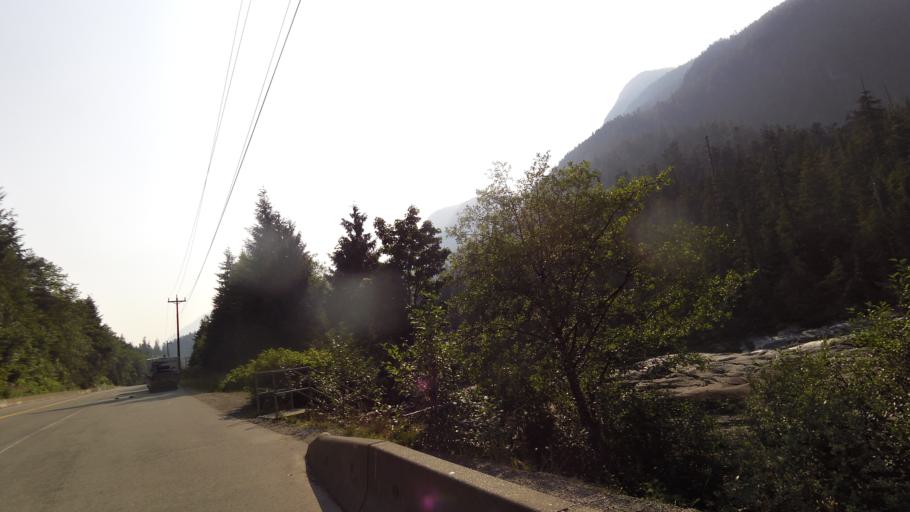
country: CA
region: British Columbia
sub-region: Regional District of Alberni-Clayoquot
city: Ucluelet
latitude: 49.2143
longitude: -125.3675
